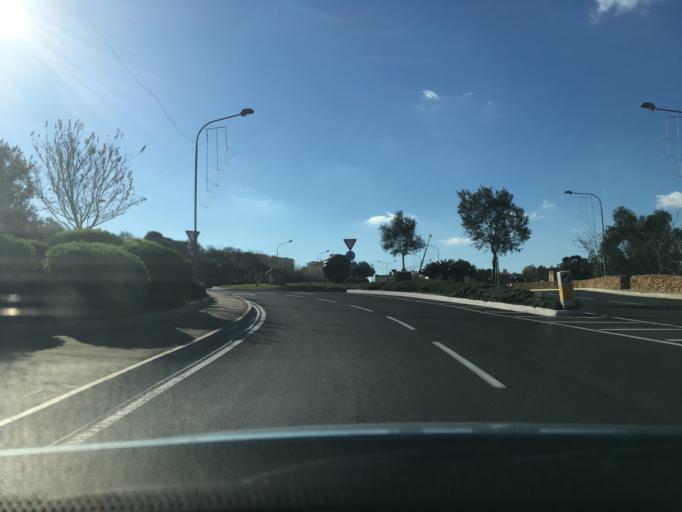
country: MT
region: Ghajnsielem
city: Mgarr
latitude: 36.0245
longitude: 14.2913
